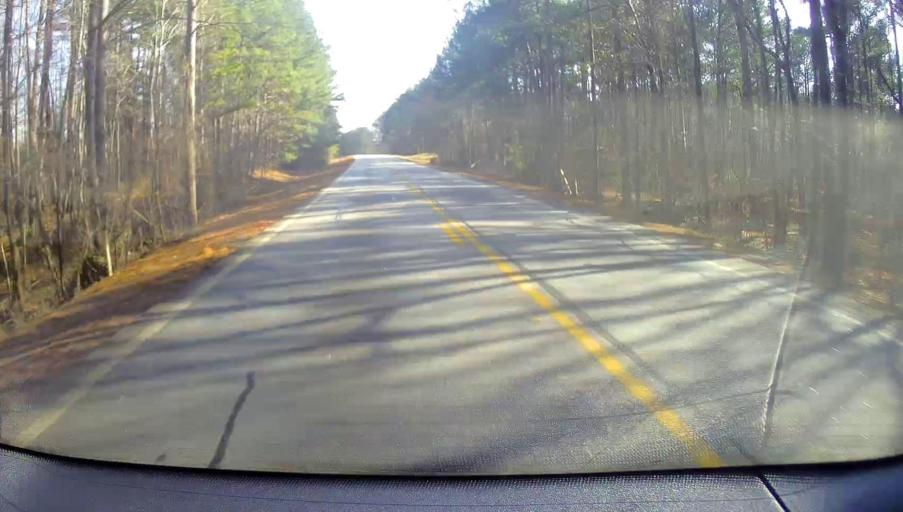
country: US
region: Georgia
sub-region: Butts County
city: Indian Springs
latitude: 33.2301
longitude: -83.8760
